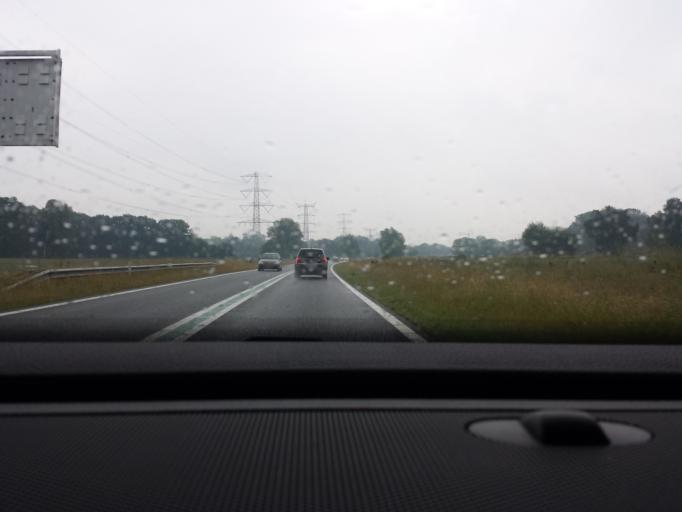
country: NL
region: Overijssel
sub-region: Gemeente Enschede
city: Enschede
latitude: 52.2028
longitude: 6.9116
